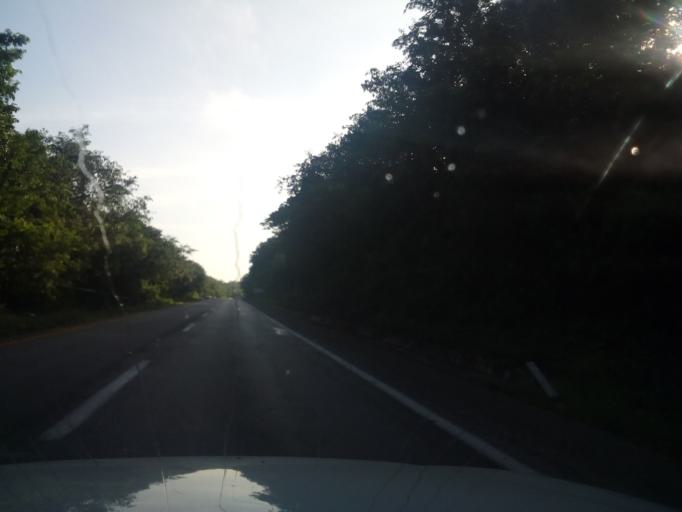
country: MX
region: Yucatan
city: Tinum
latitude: 20.7142
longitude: -88.4214
